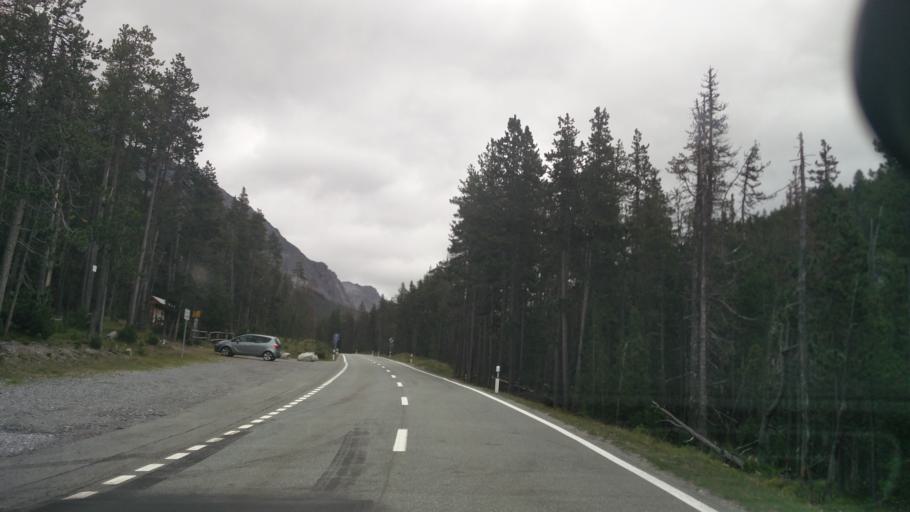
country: CH
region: Grisons
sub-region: Inn District
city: Zernez
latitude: 46.6617
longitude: 10.2225
